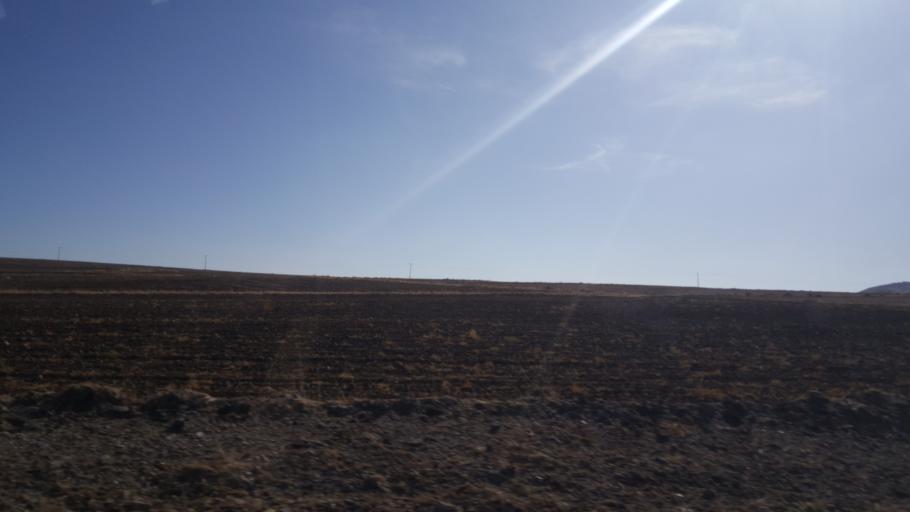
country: TR
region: Ankara
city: Altpinar
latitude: 39.2416
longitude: 32.7246
